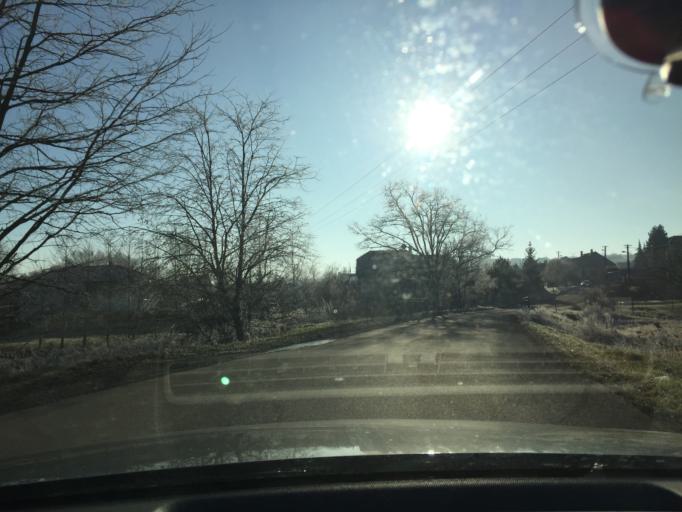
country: CZ
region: Central Bohemia
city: Trebotov
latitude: 49.9985
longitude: 14.2663
